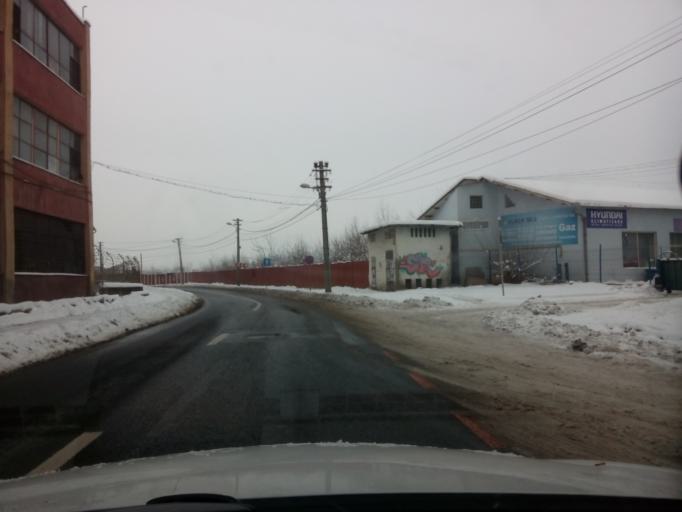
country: RO
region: Sibiu
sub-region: Municipiul Sibiu
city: Sibiu
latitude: 45.8026
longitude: 24.1565
